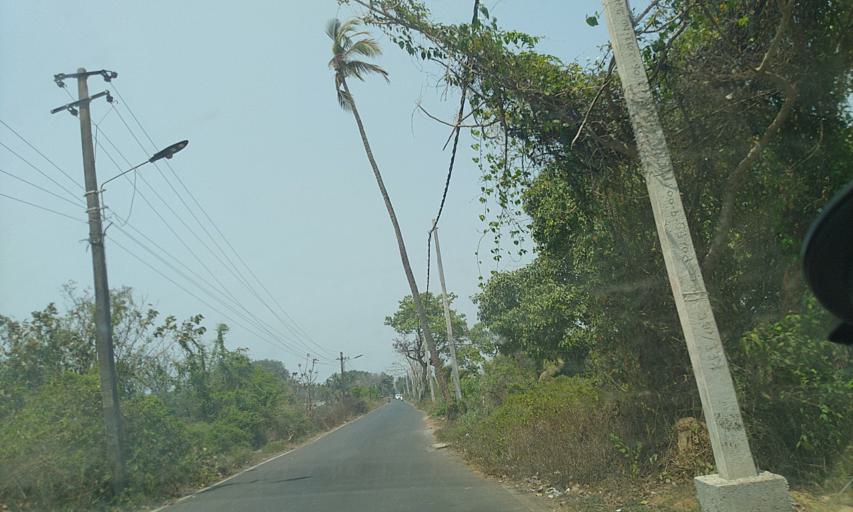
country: IN
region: Goa
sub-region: North Goa
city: Saligao
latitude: 15.5480
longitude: 73.8062
